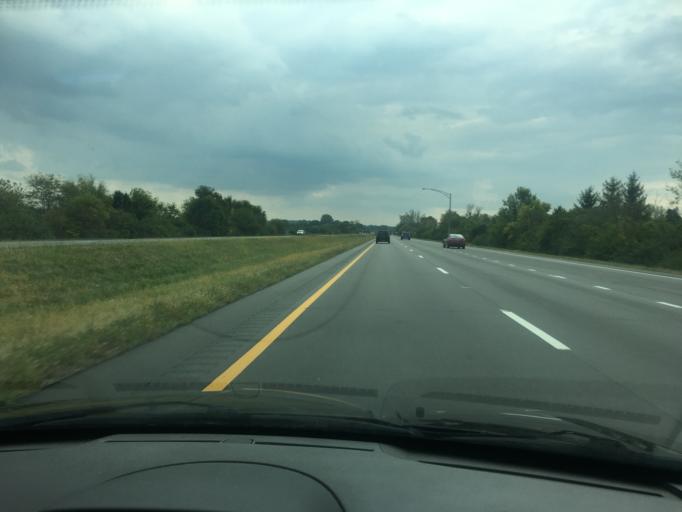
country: US
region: Ohio
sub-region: Clark County
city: Northridge
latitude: 39.9819
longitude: -83.8146
